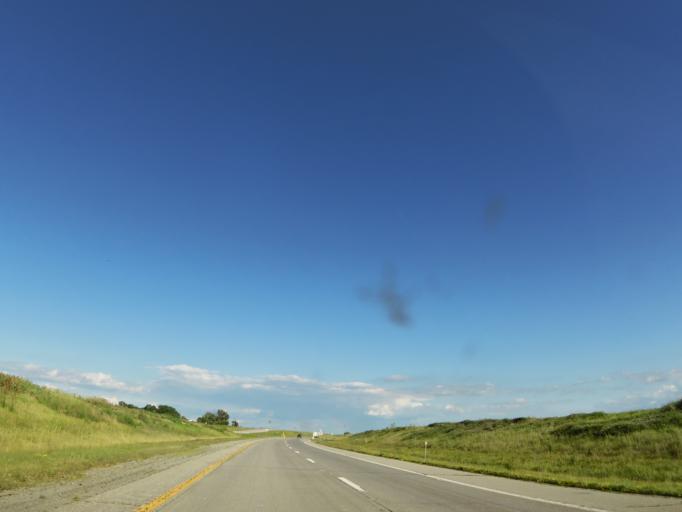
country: US
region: Missouri
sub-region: Pike County
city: Bowling Green
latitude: 39.3047
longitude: -91.1211
